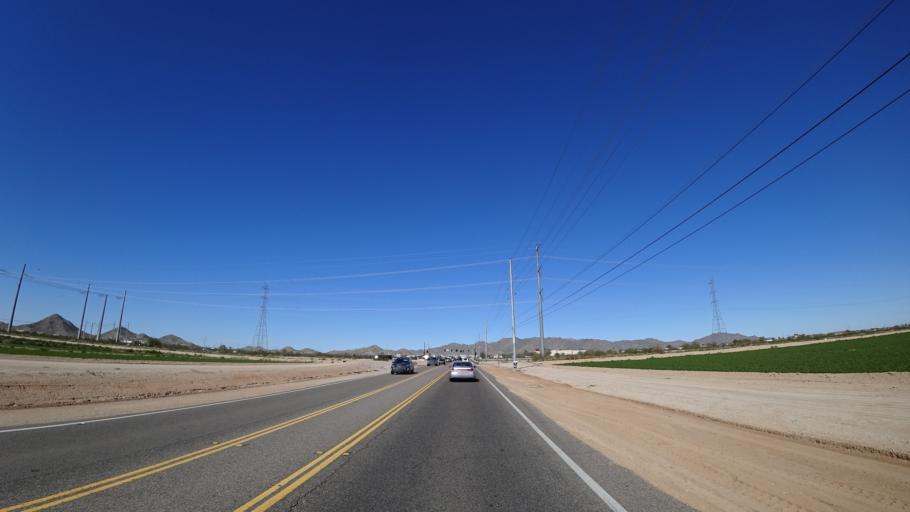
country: US
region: Arizona
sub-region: Maricopa County
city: Buckeye
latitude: 33.4190
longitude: -112.5909
